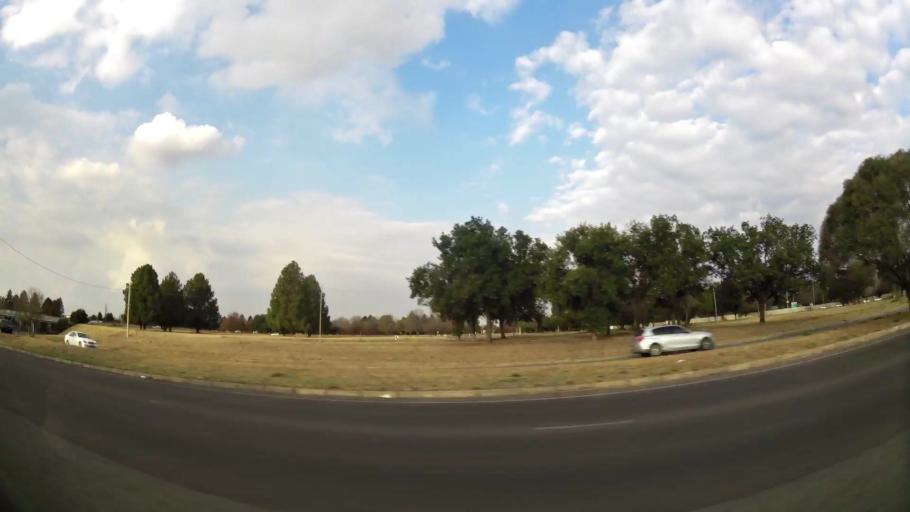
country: ZA
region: Orange Free State
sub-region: Fezile Dabi District Municipality
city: Sasolburg
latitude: -26.8021
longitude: 27.8310
